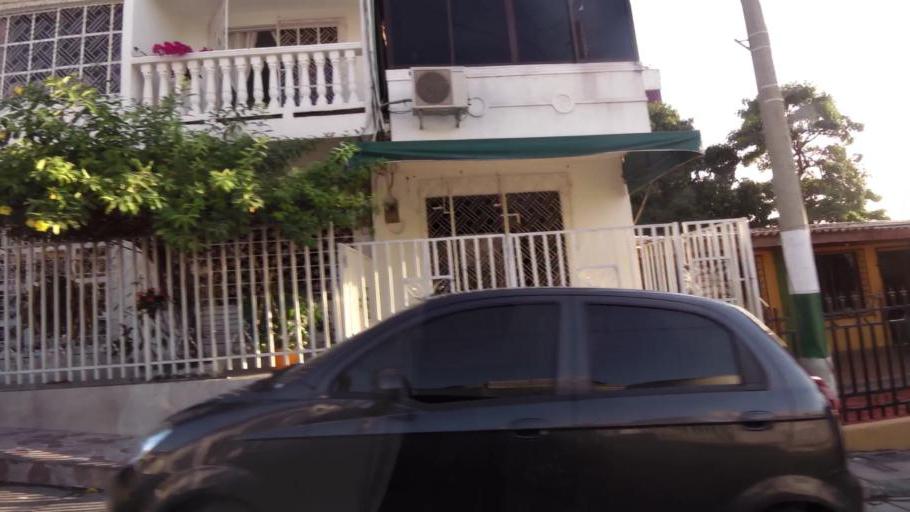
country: CO
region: Bolivar
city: Cartagena
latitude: 10.3929
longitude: -75.5194
